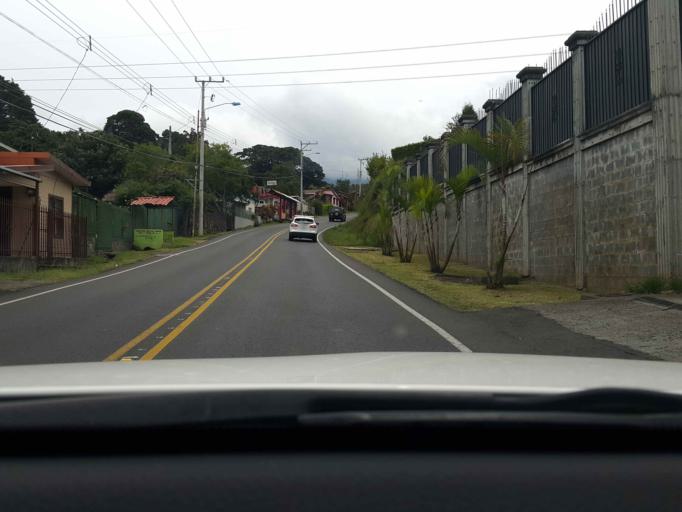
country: CR
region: Heredia
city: San Josecito
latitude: 10.0295
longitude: -84.0936
